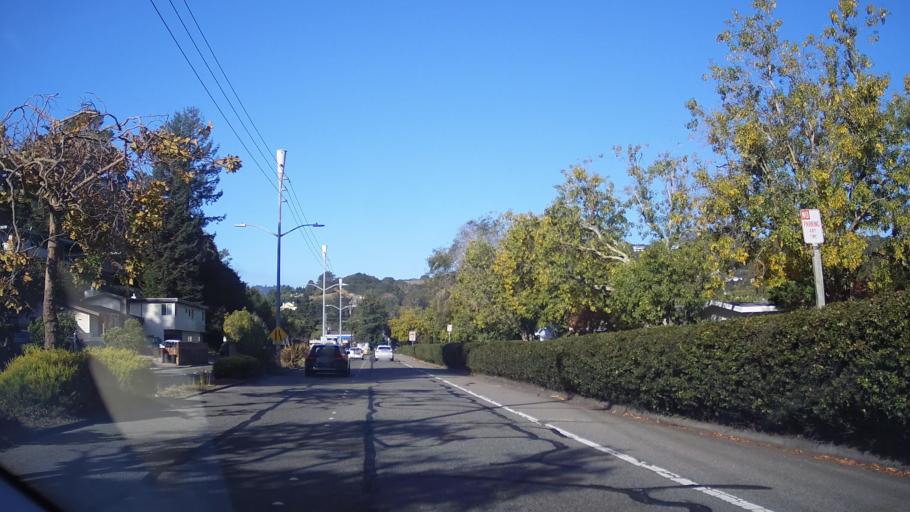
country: US
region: California
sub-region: Marin County
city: Strawberry
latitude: 37.9038
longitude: -122.5200
